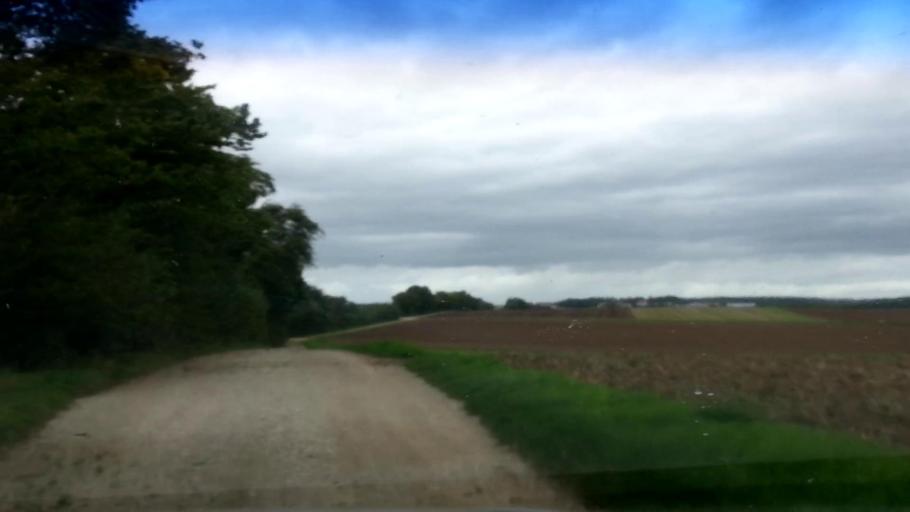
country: DE
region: Bavaria
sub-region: Upper Franconia
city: Memmelsdorf
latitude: 49.9675
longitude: 10.9683
